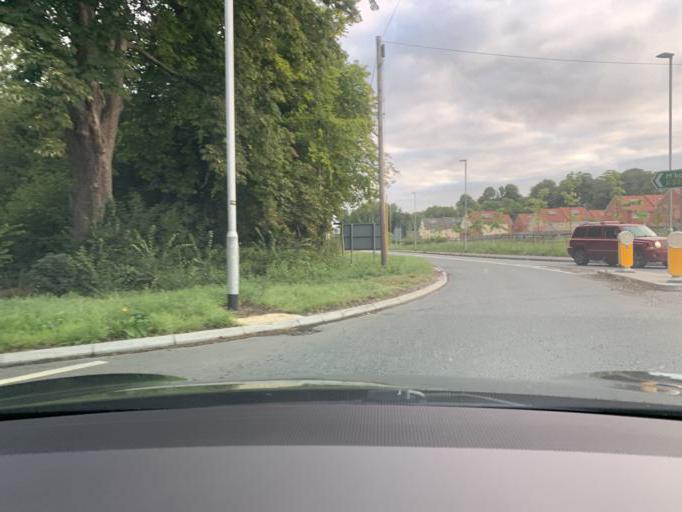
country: GB
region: England
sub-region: Wiltshire
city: Tidworth
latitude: 51.2269
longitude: -1.6640
